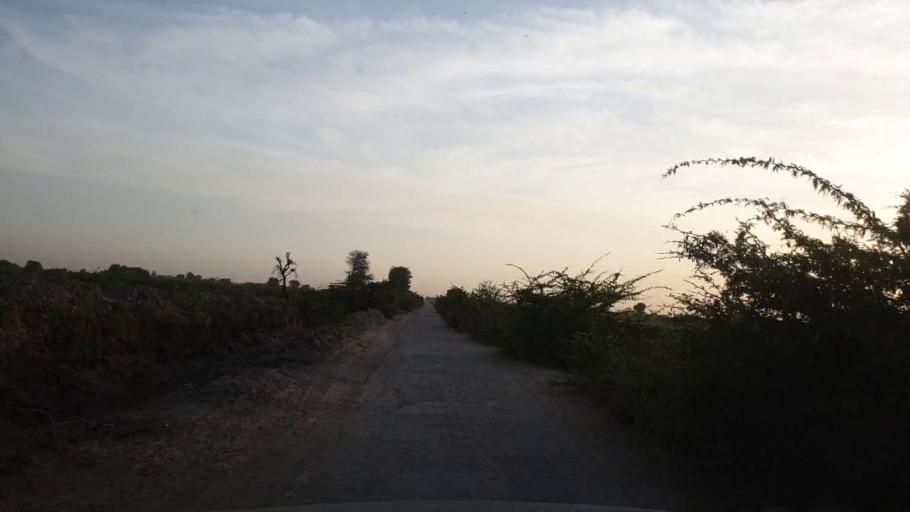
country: PK
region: Sindh
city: Kunri
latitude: 25.1234
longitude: 69.5690
